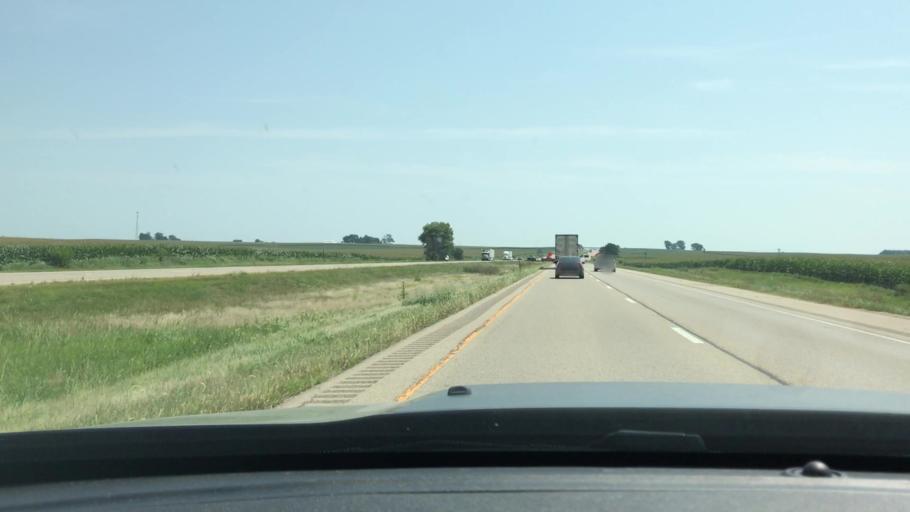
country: US
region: Illinois
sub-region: Bureau County
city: Depue
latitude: 41.3998
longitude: -89.3460
